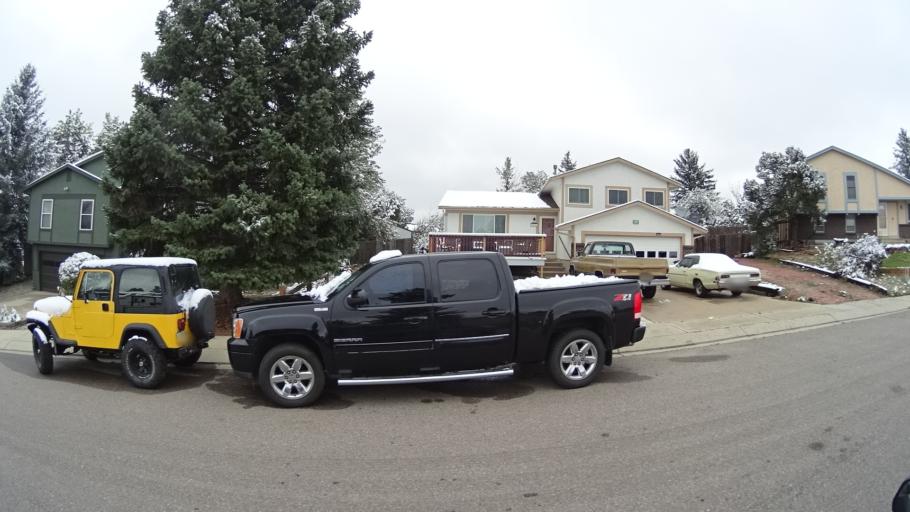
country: US
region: Colorado
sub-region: El Paso County
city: Cimarron Hills
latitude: 38.9193
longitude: -104.7725
